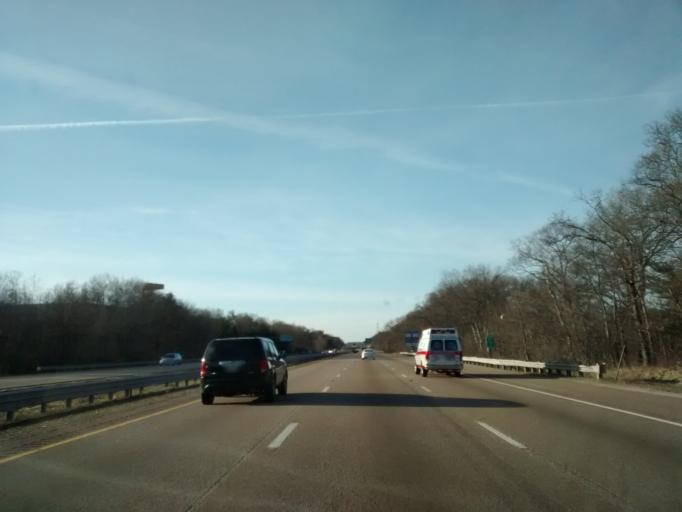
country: US
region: Massachusetts
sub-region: Norfolk County
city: Avon
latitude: 42.1351
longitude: -71.0642
